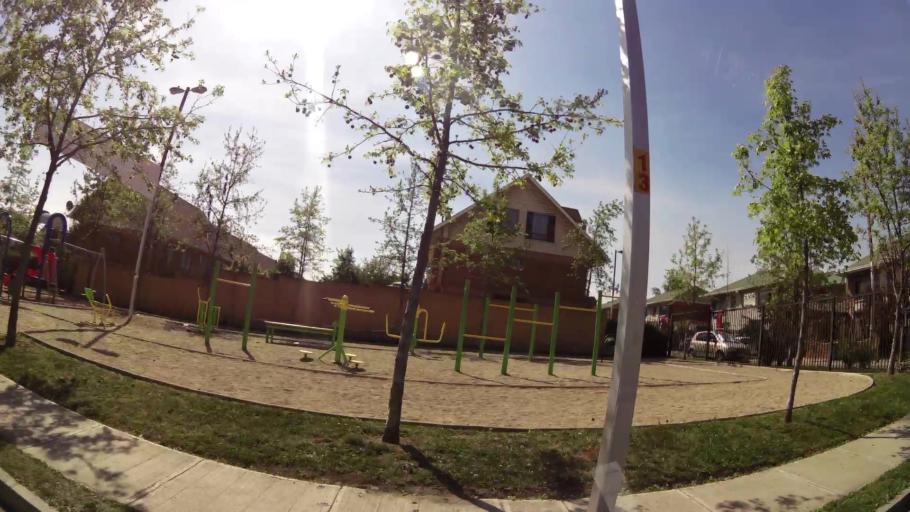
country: CL
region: Santiago Metropolitan
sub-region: Provincia de Cordillera
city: Puente Alto
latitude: -33.5399
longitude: -70.5500
